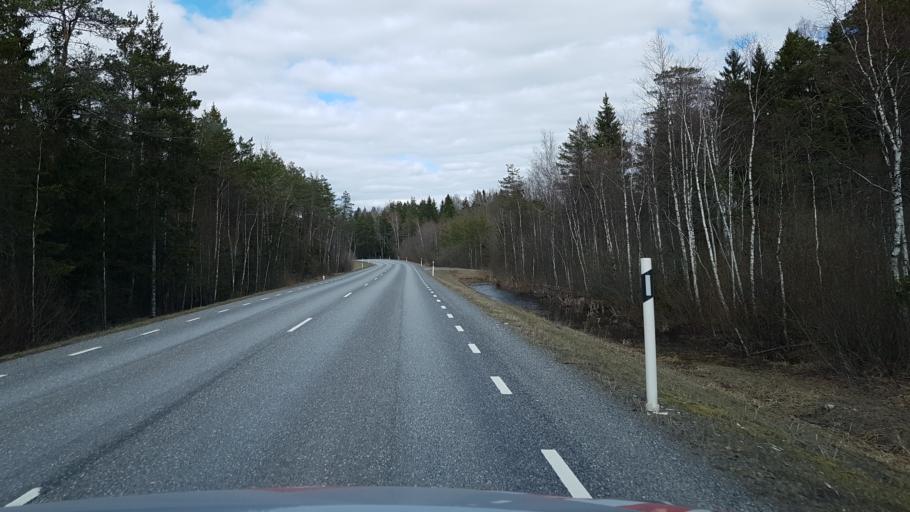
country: EE
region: Laeaene-Virumaa
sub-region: Rakke vald
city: Rakke
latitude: 59.0365
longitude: 26.2391
